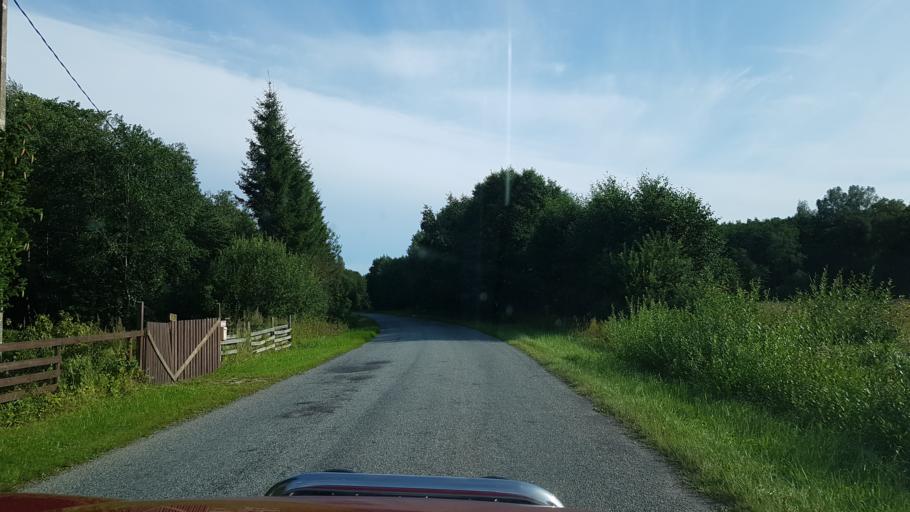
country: EE
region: Laeaene
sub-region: Lihula vald
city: Lihula
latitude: 58.4135
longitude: 24.0142
